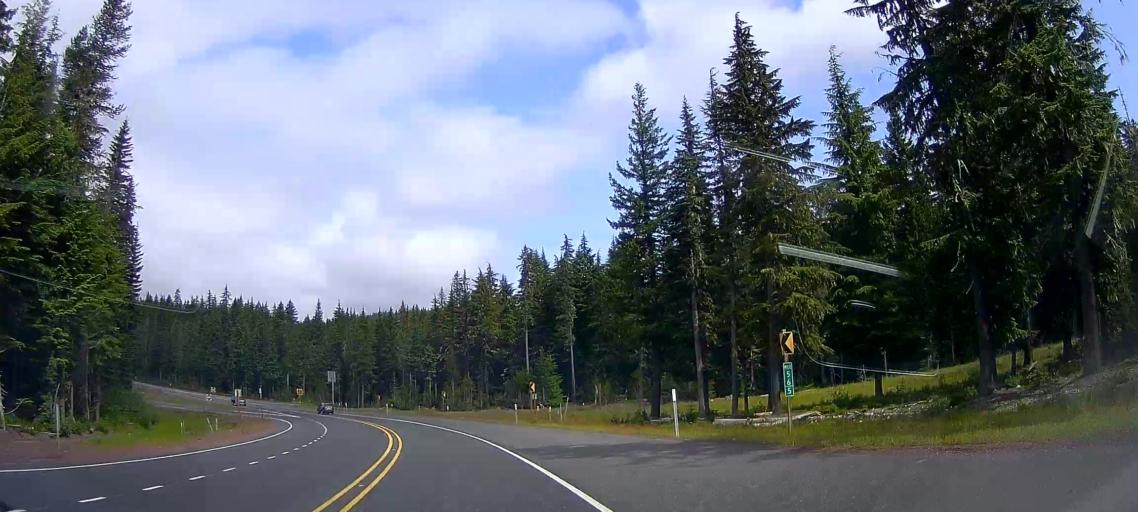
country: US
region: Oregon
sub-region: Clackamas County
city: Mount Hood Village
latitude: 45.2837
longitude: -121.7144
